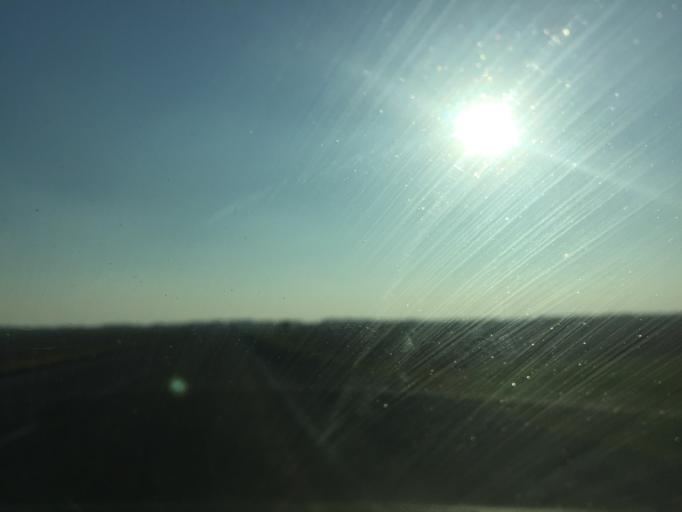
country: BY
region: Gomel
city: Dobrush
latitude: 52.3146
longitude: 31.2440
